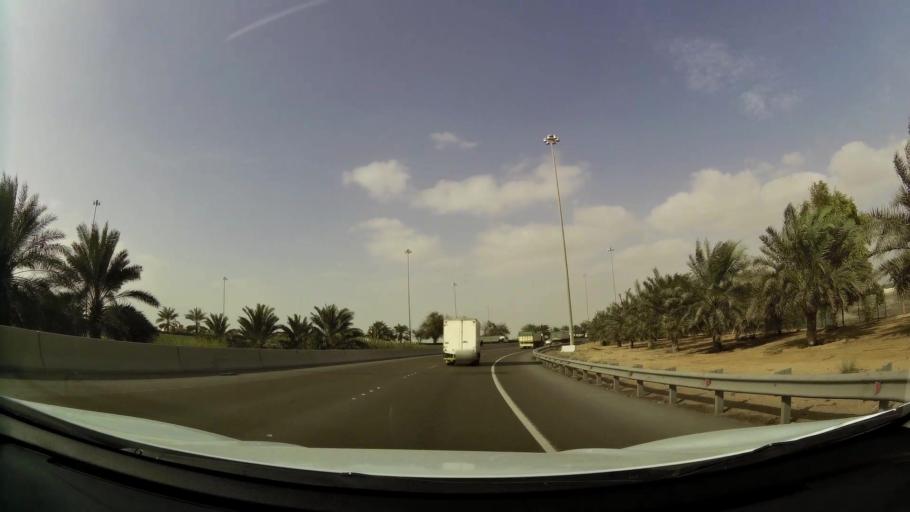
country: AE
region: Abu Dhabi
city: Abu Dhabi
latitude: 24.4152
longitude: 54.5065
